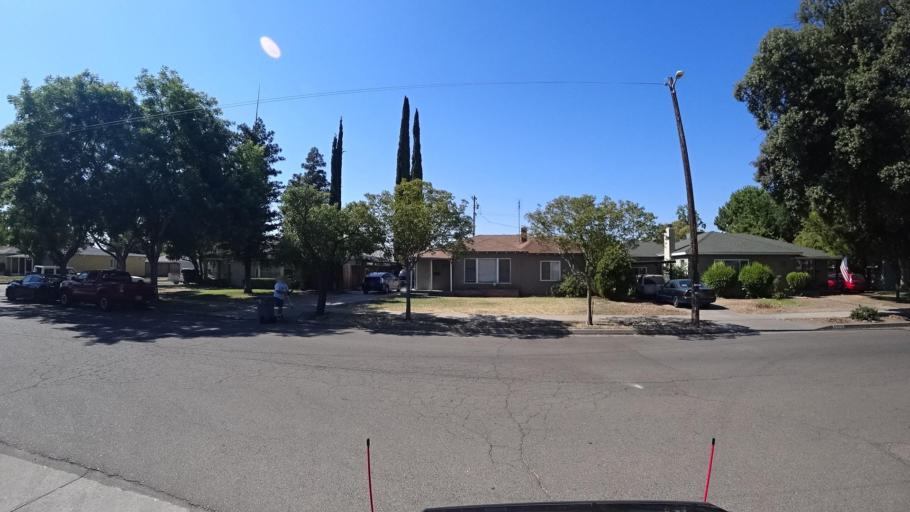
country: US
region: California
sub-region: Fresno County
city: Fresno
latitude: 36.7786
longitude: -119.7753
